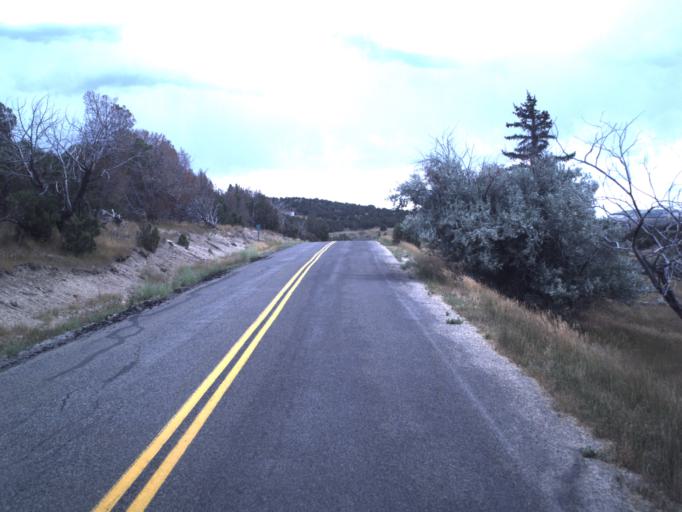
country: US
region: Utah
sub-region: Summit County
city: Oakley
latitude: 40.7791
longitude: -111.3917
